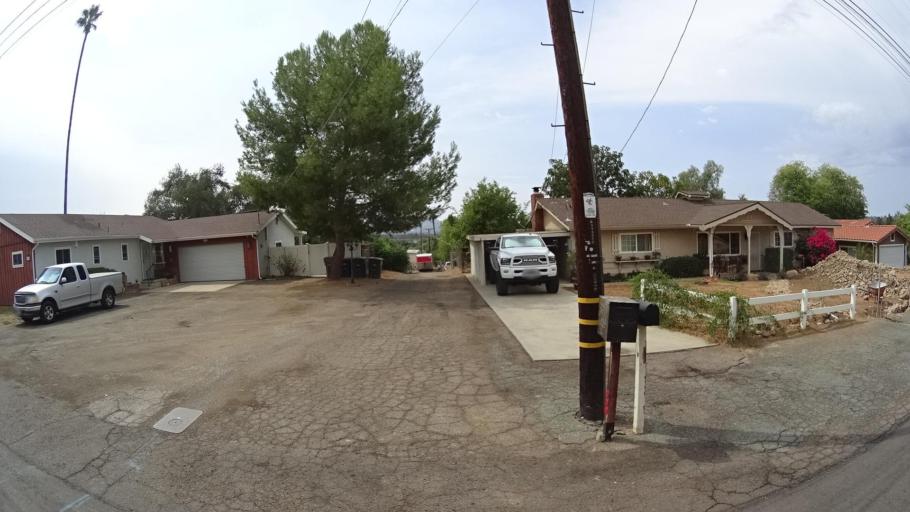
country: US
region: California
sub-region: San Diego County
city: Ramona
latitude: 33.0401
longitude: -116.8604
